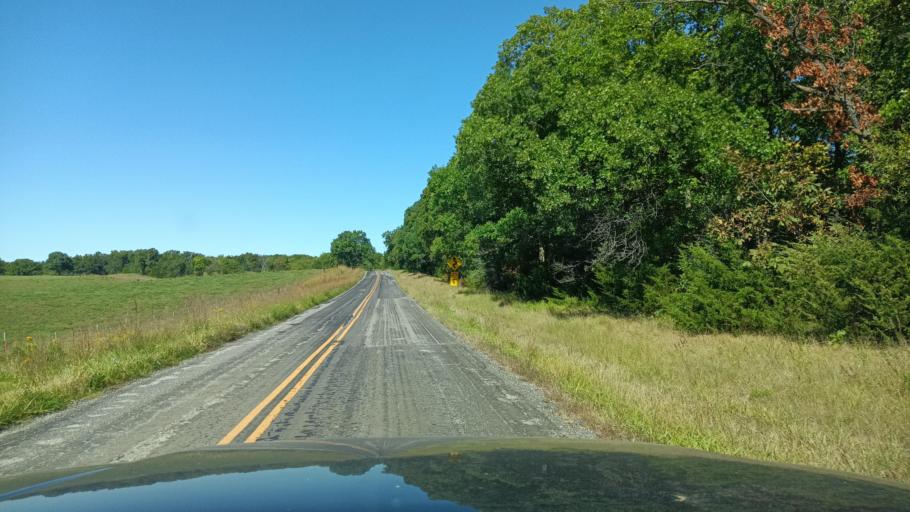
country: US
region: Missouri
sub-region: Scotland County
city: Memphis
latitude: 40.3525
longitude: -92.3451
